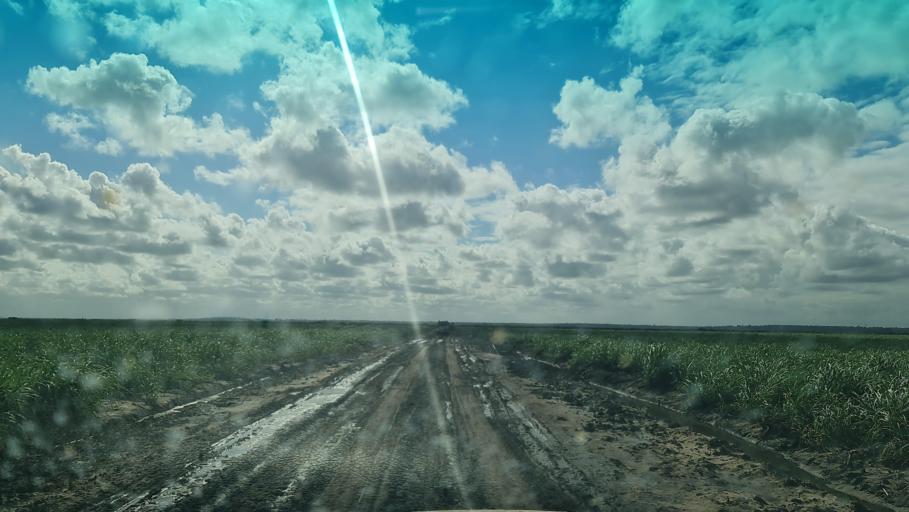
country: MZ
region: Maputo
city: Manhica
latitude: -25.4391
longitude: 32.8578
